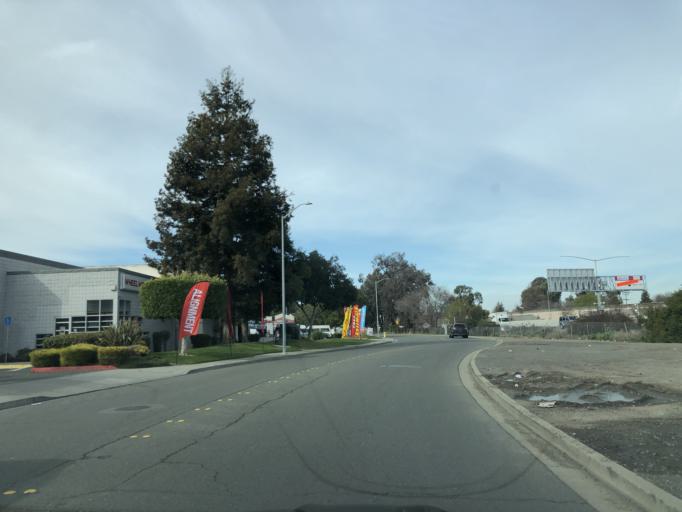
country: US
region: California
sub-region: Alameda County
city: Fremont
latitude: 37.5181
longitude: -121.9817
